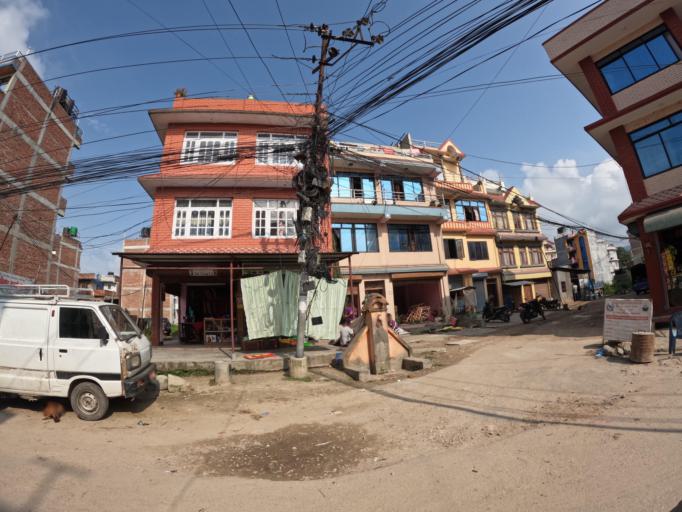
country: NP
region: Central Region
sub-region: Bagmati Zone
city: Bhaktapur
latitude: 27.6805
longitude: 85.4455
